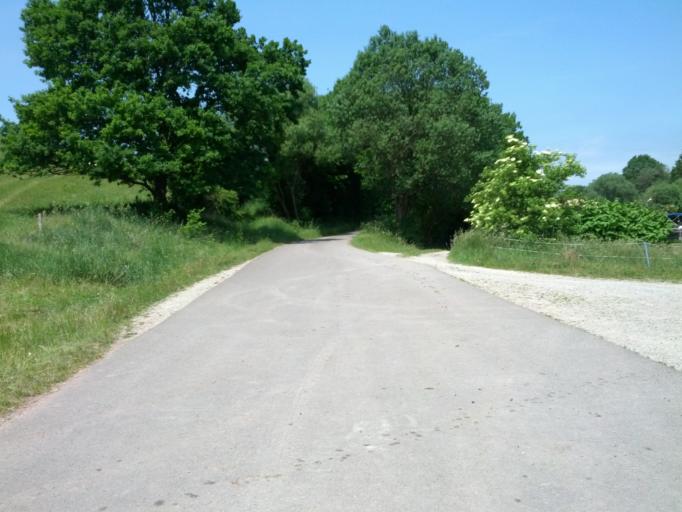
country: DE
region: Thuringia
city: Wiesenthal
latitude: 50.7124
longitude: 10.1664
